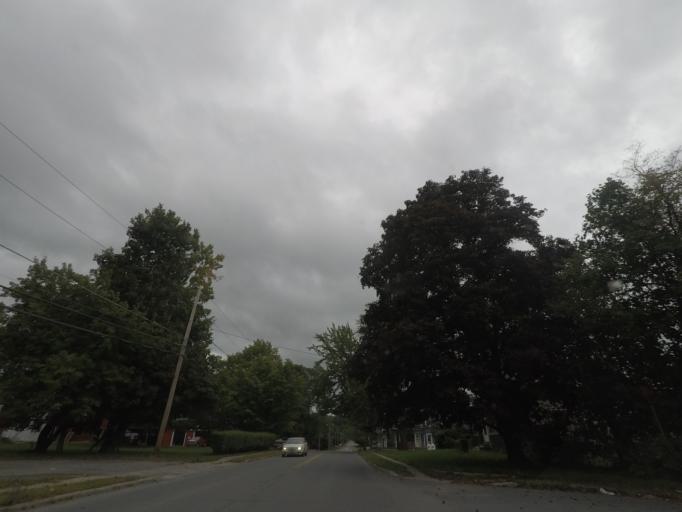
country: US
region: New York
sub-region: Saratoga County
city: Mechanicville
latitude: 42.9049
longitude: -73.6808
